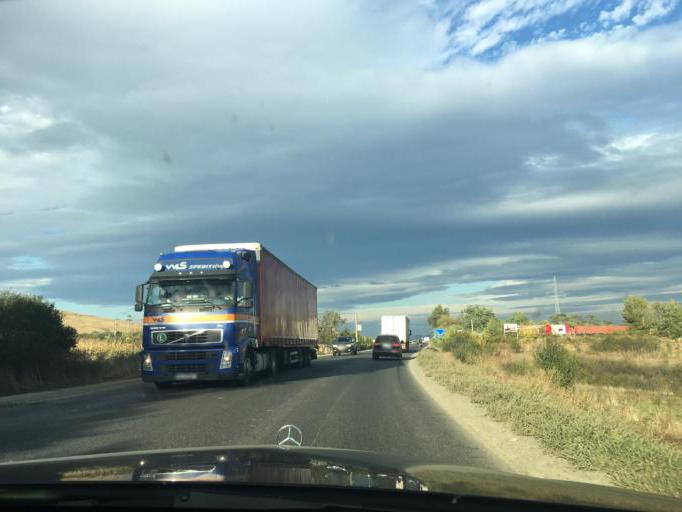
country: RO
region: Alba
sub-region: Municipiul Alba Iulia
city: Barabant
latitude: 46.1116
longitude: 23.6121
